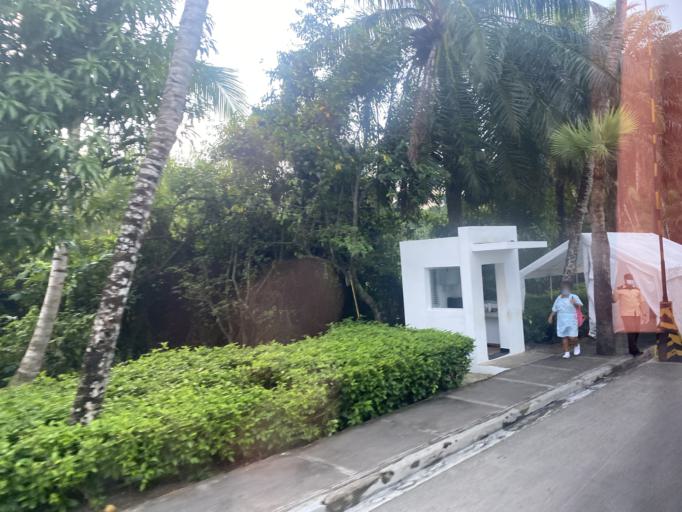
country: DO
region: San Juan
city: Punta Cana
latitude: 18.7168
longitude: -68.4580
